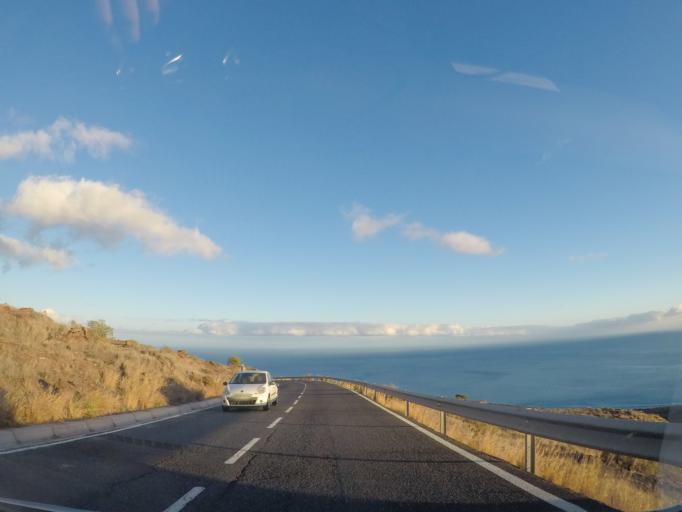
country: ES
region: Canary Islands
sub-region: Provincia de Santa Cruz de Tenerife
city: Alajero
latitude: 28.0400
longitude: -17.2301
